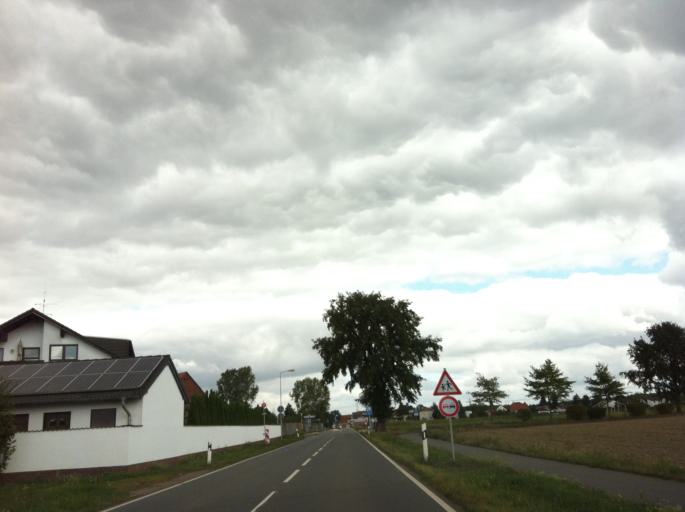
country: DE
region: Hesse
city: Pfungstadt
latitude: 49.8033
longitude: 8.5633
